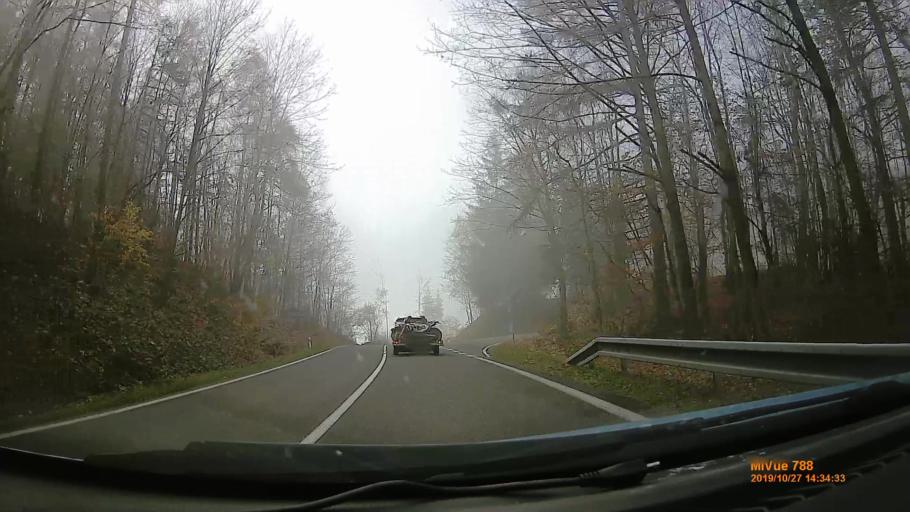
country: CZ
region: Olomoucky
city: Stity
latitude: 49.9881
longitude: 16.8059
